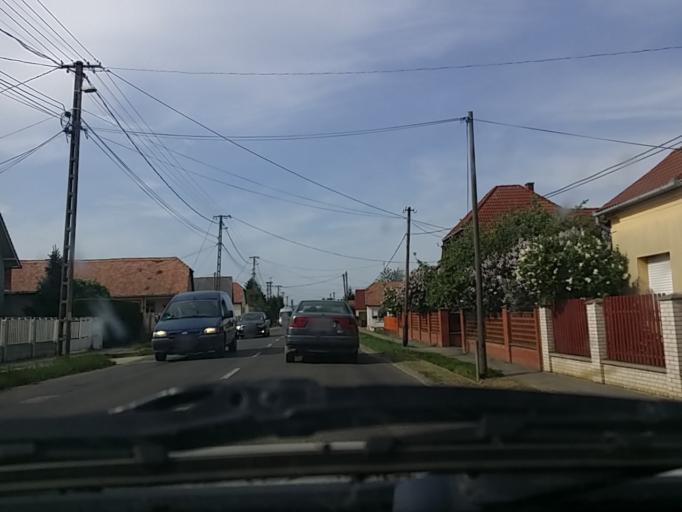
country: HU
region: Baranya
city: Harkany
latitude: 45.9462
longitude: 18.2377
